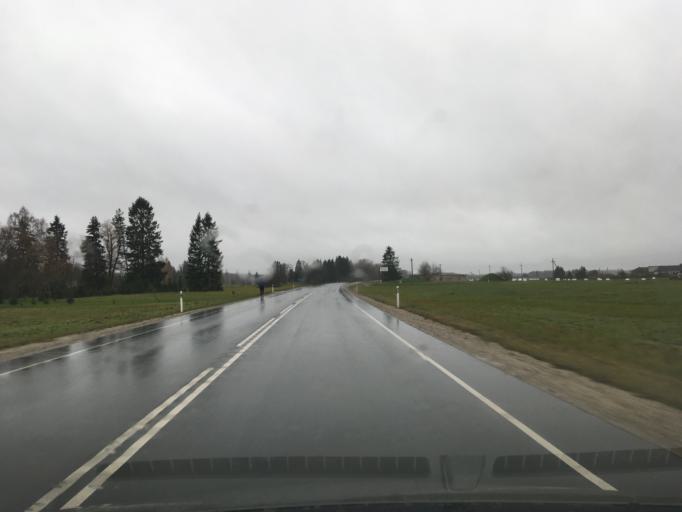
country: EE
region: Harju
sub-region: Nissi vald
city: Turba
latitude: 58.8763
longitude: 24.0866
